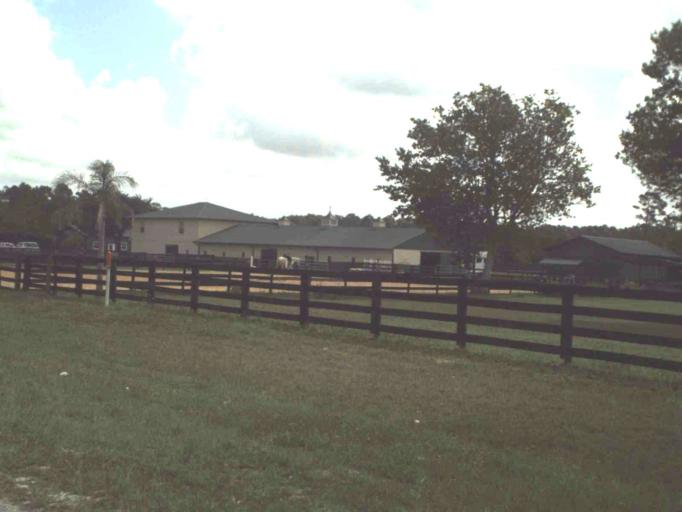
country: US
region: Florida
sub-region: Volusia County
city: Samsula-Spruce Creek
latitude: 28.9970
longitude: -81.0711
